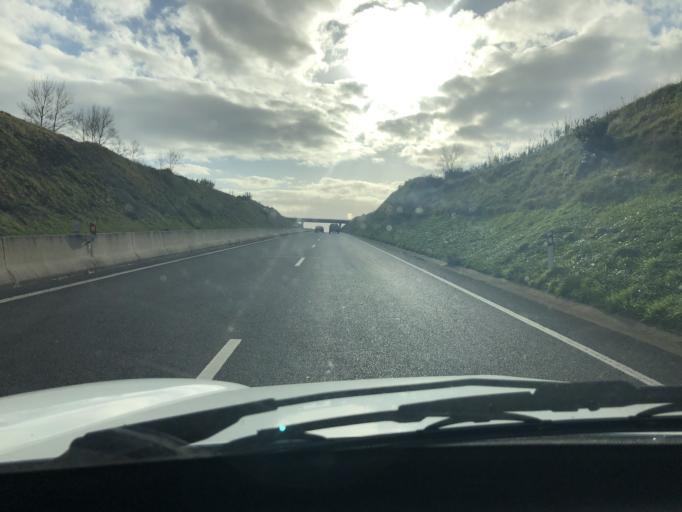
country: PT
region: Azores
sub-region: Ribeira Grande
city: Rabo de Peixe
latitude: 37.7324
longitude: -25.5410
